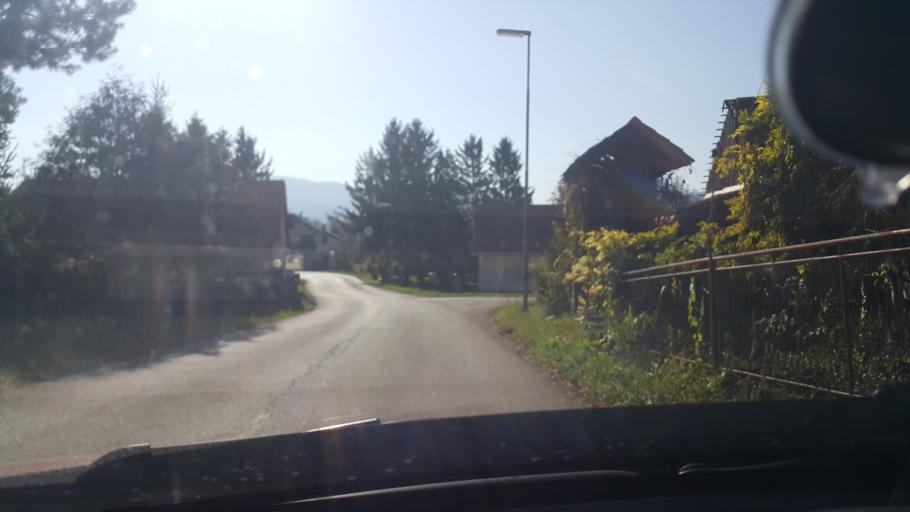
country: SI
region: Brezice
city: Brezice
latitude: 45.9075
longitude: 15.6329
